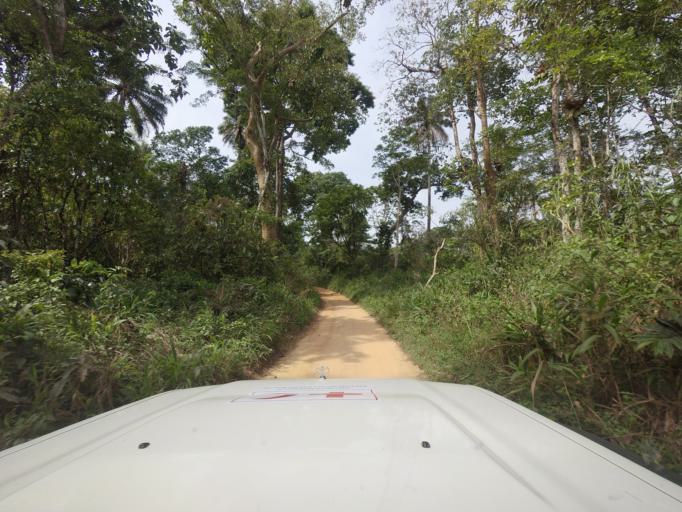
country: GN
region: Nzerekore
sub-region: Macenta
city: Macenta
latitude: 8.4655
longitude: -9.5779
